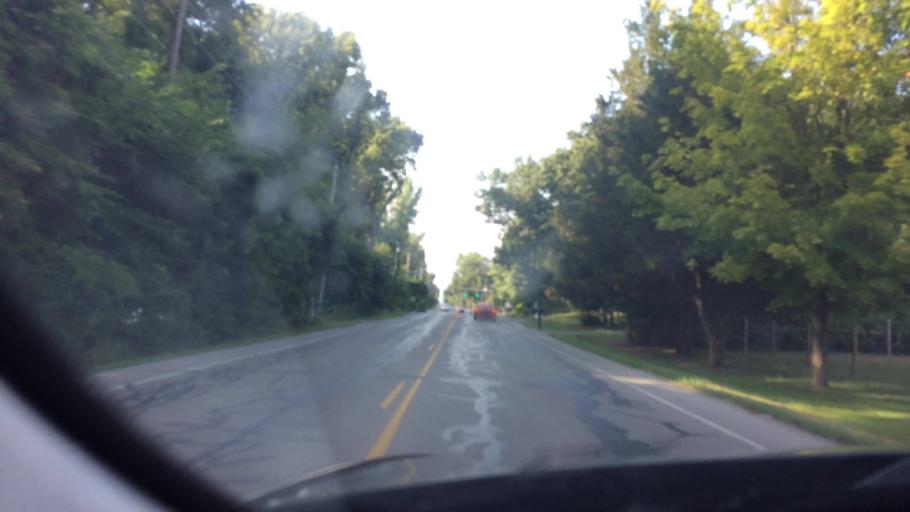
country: US
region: Ohio
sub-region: Lucas County
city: Holland
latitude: 41.6572
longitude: -83.7222
